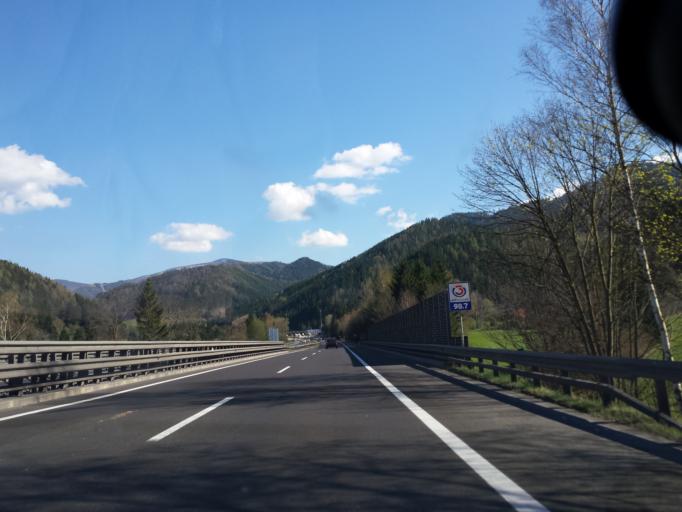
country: AT
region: Styria
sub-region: Politischer Bezirk Leoben
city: Sankt Michael in Obersteiermark
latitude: 47.3300
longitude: 15.0242
